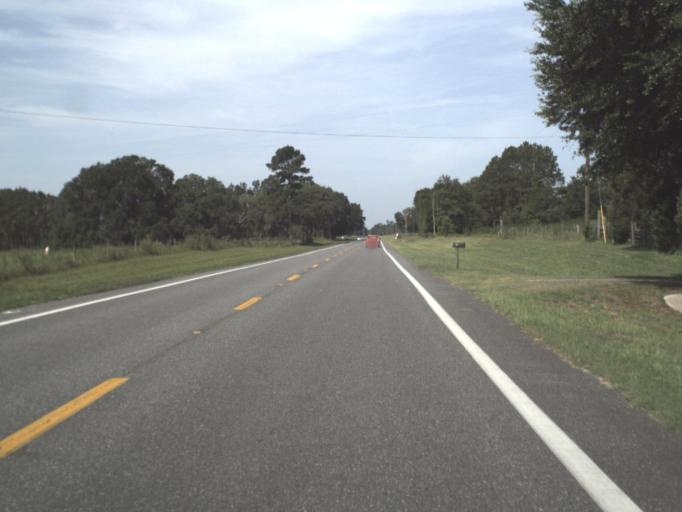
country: US
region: Florida
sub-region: Suwannee County
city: Live Oak
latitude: 30.2133
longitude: -83.0851
